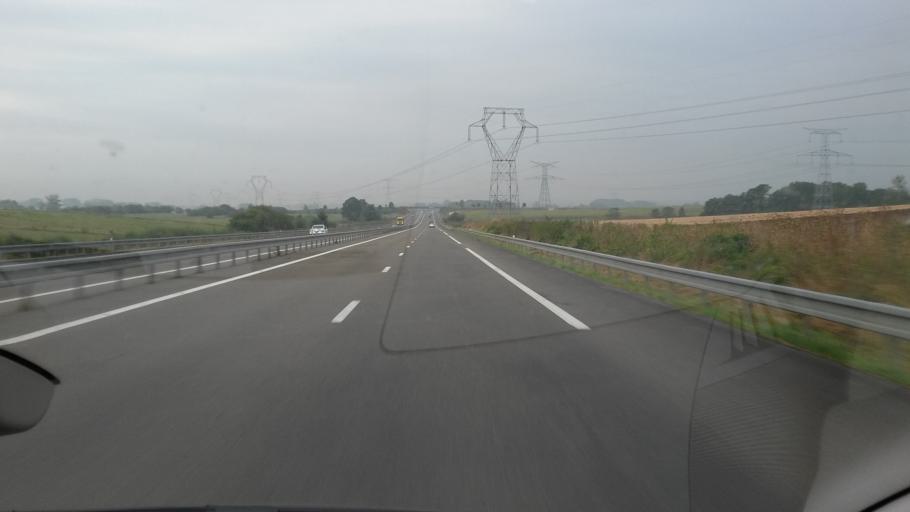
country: FR
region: Champagne-Ardenne
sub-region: Departement des Ardennes
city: Rethel
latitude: 49.5730
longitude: 4.4765
